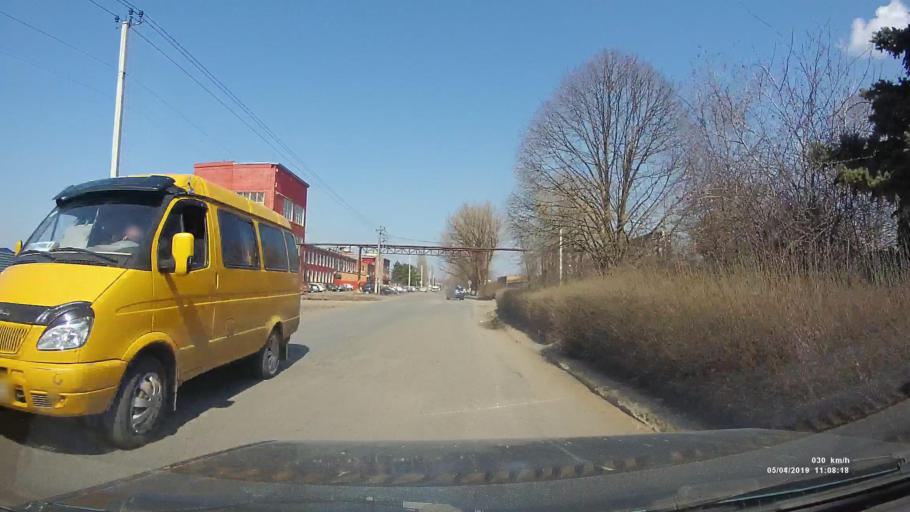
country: RU
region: Rostov
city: Azov
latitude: 47.0852
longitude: 39.4358
